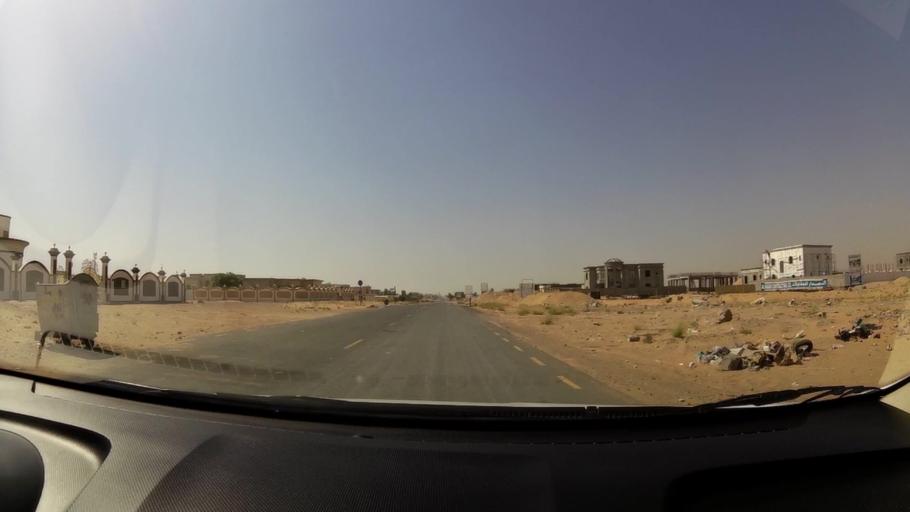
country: AE
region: Umm al Qaywayn
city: Umm al Qaywayn
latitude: 25.4742
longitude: 55.6177
